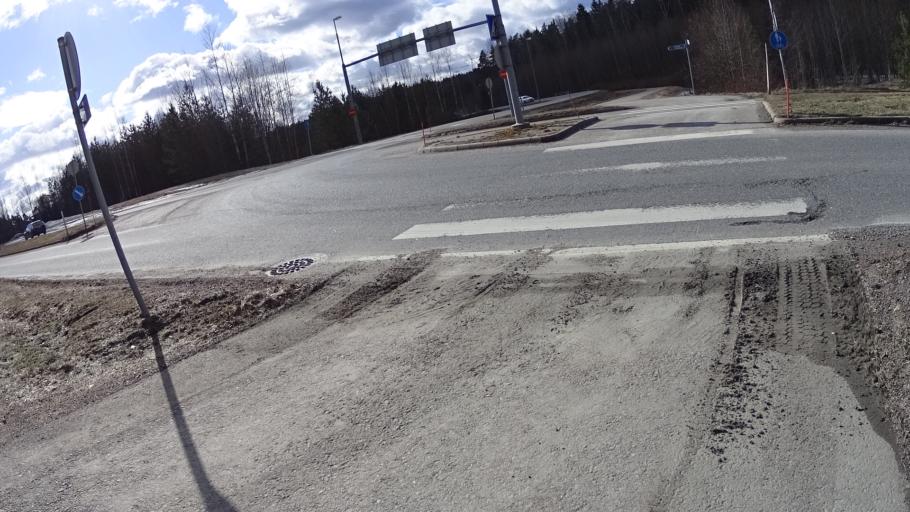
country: FI
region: Uusimaa
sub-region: Helsinki
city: Kauniainen
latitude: 60.2635
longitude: 24.7314
